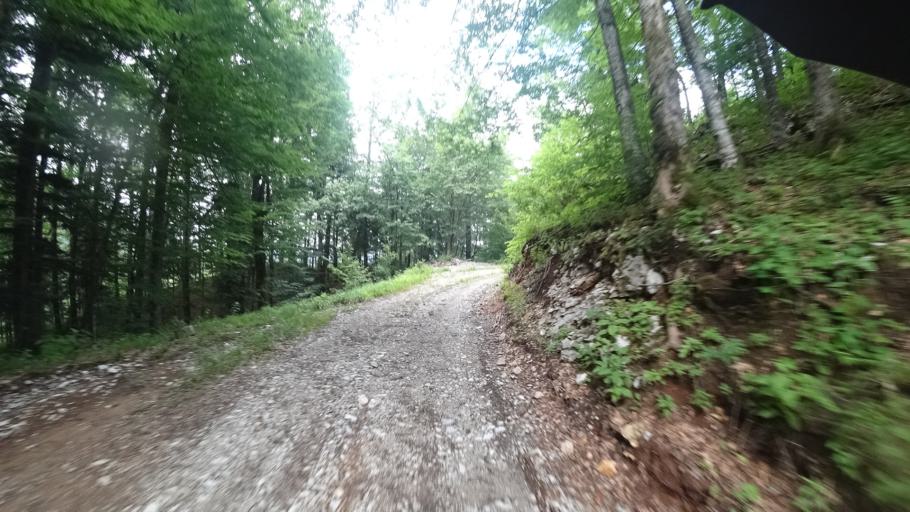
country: SI
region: Osilnica
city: Osilnica
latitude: 45.4926
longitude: 14.6729
